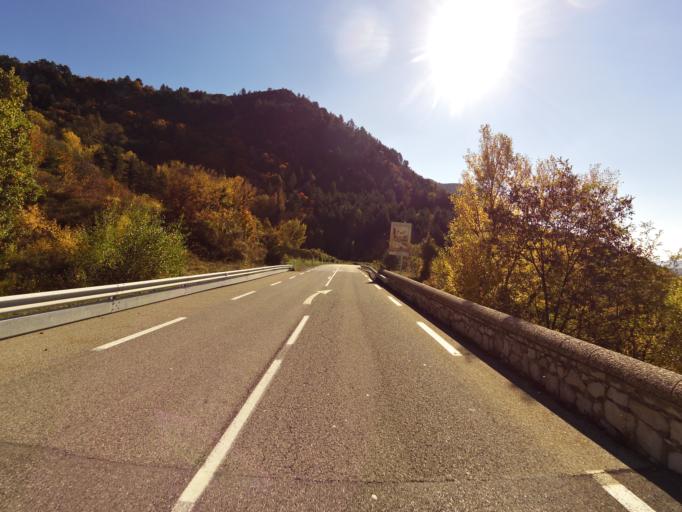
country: FR
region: Rhone-Alpes
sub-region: Departement de l'Ardeche
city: Vesseaux
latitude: 44.7004
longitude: 4.4818
